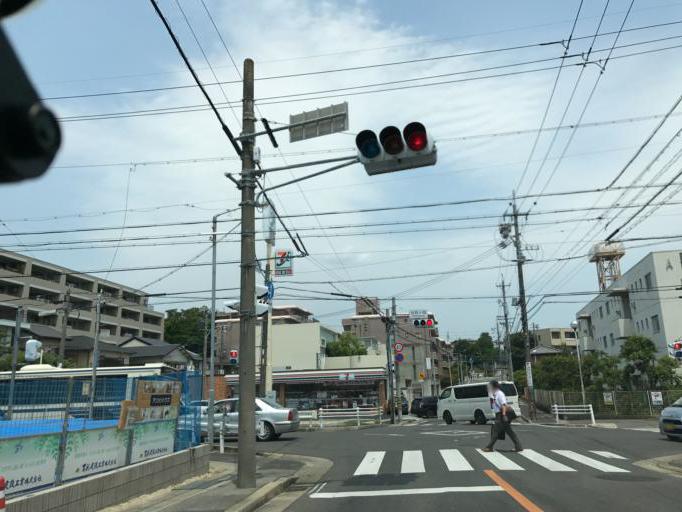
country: JP
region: Aichi
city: Nagoya-shi
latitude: 35.1288
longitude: 136.9588
